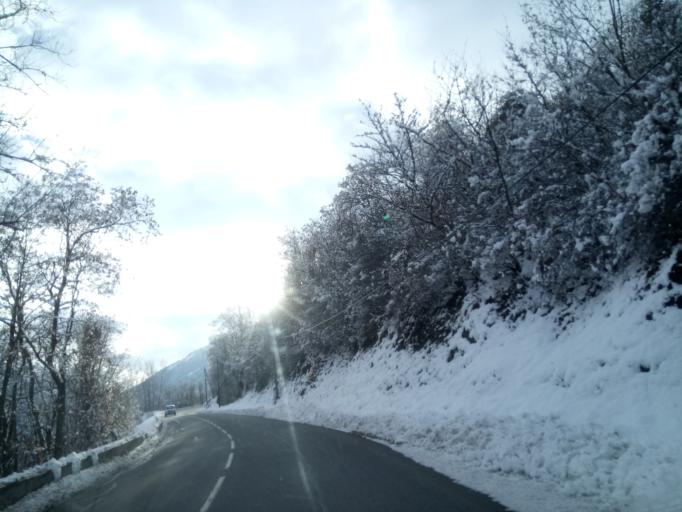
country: FR
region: Rhone-Alpes
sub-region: Departement de la Savoie
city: Saint-Jean-de-Maurienne
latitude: 45.2641
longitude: 6.3288
